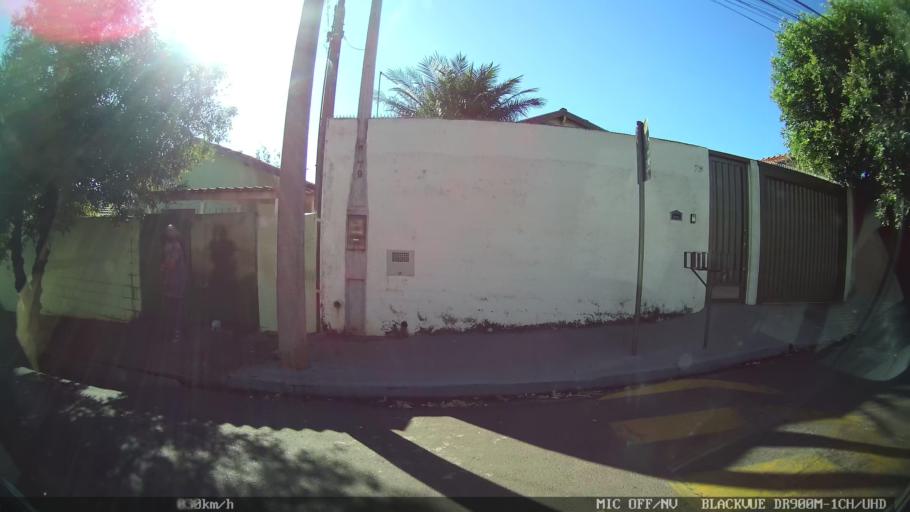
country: BR
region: Sao Paulo
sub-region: Olimpia
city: Olimpia
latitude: -20.7406
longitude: -48.9021
